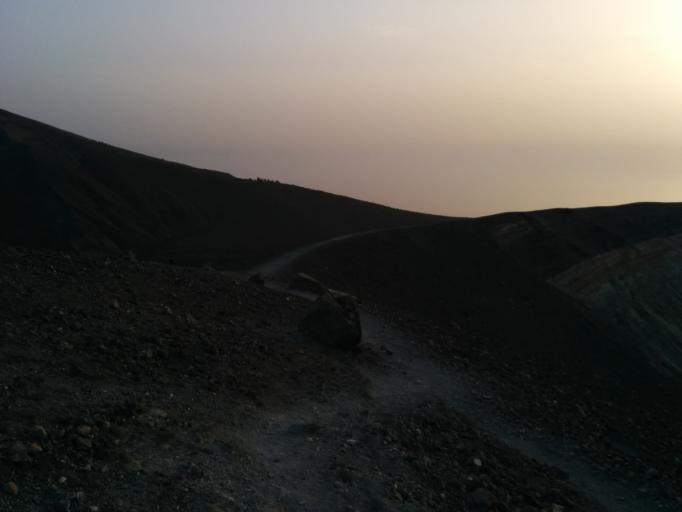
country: IT
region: Sicily
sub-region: Messina
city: Lipari
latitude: 38.4032
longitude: 14.9651
